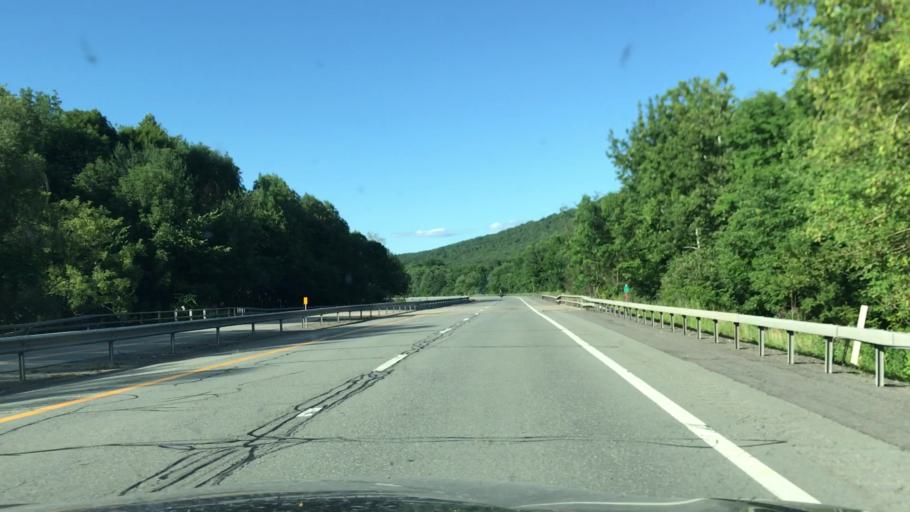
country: US
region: New York
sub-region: Delaware County
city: Hancock
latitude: 41.9810
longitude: -75.1672
